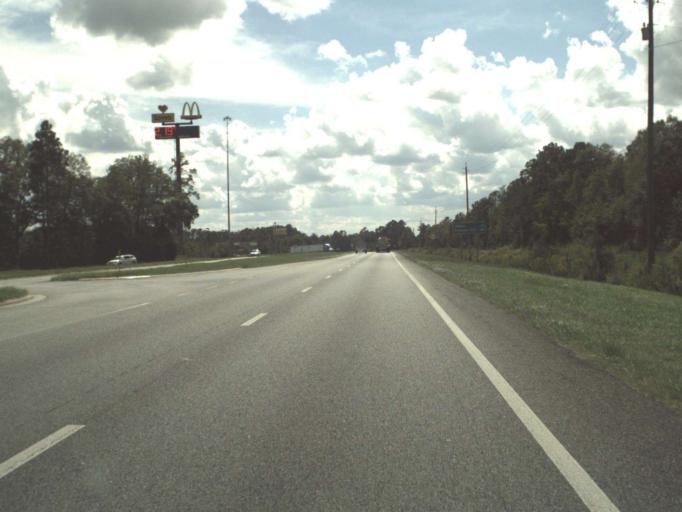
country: US
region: Florida
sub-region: Jackson County
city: Marianna
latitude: 30.7520
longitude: -85.3825
